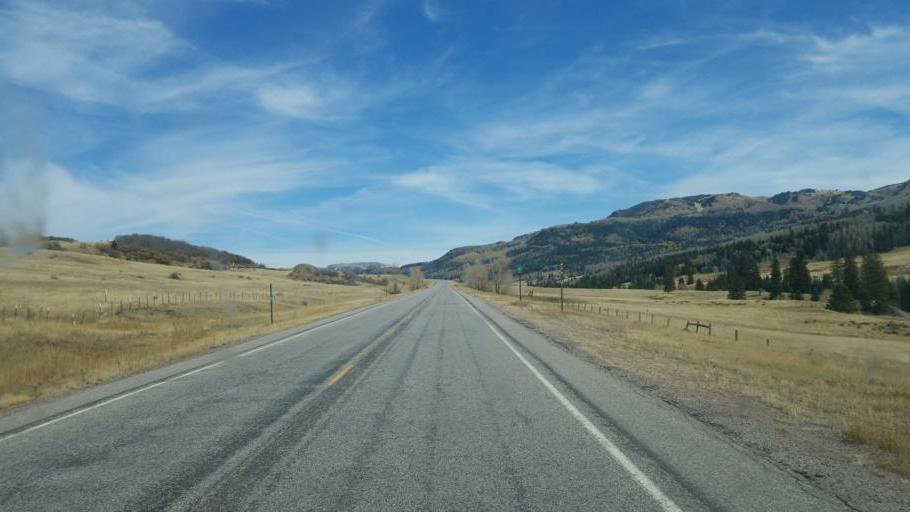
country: US
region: New Mexico
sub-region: Rio Arriba County
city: Chama
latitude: 36.9637
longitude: -106.5232
